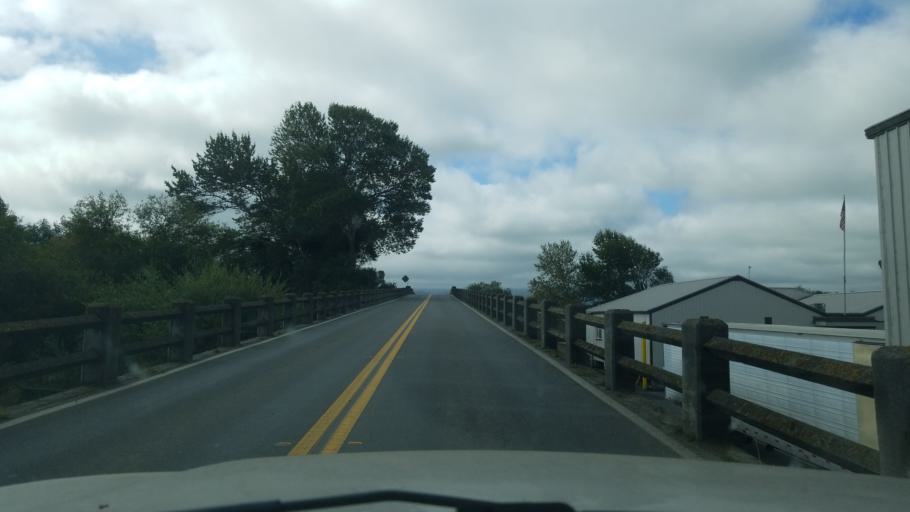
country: US
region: California
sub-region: Humboldt County
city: Fortuna
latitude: 40.6156
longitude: -124.2022
